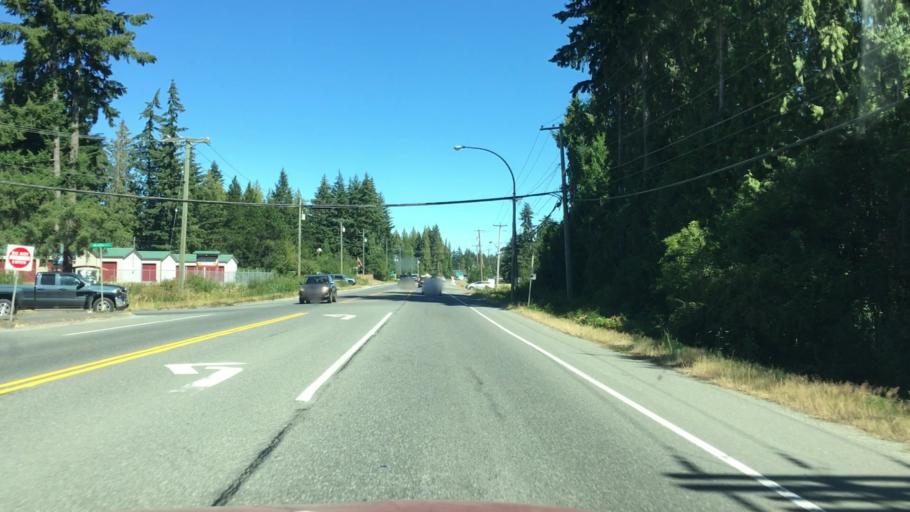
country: CA
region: British Columbia
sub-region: Regional District of Nanaimo
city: Parksville
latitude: 49.3065
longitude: -124.4837
